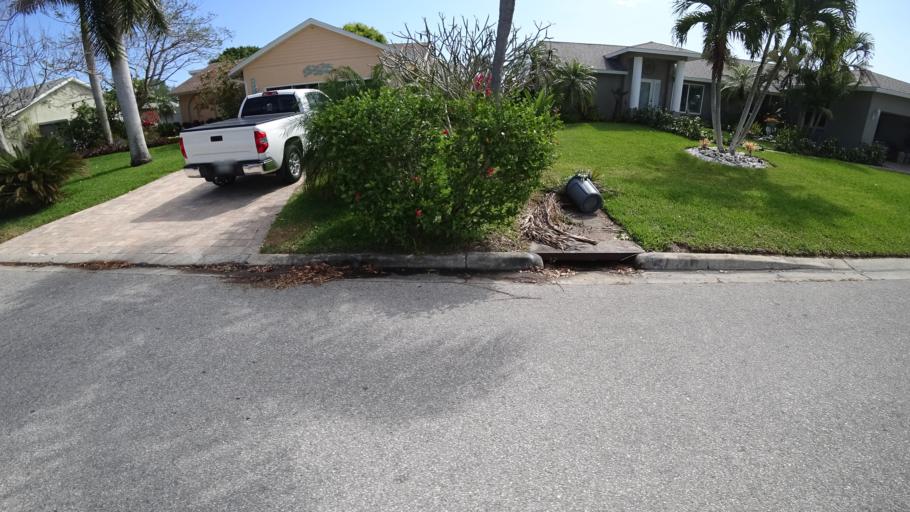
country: US
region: Florida
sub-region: Manatee County
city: Cortez
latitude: 27.4562
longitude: -82.6528
